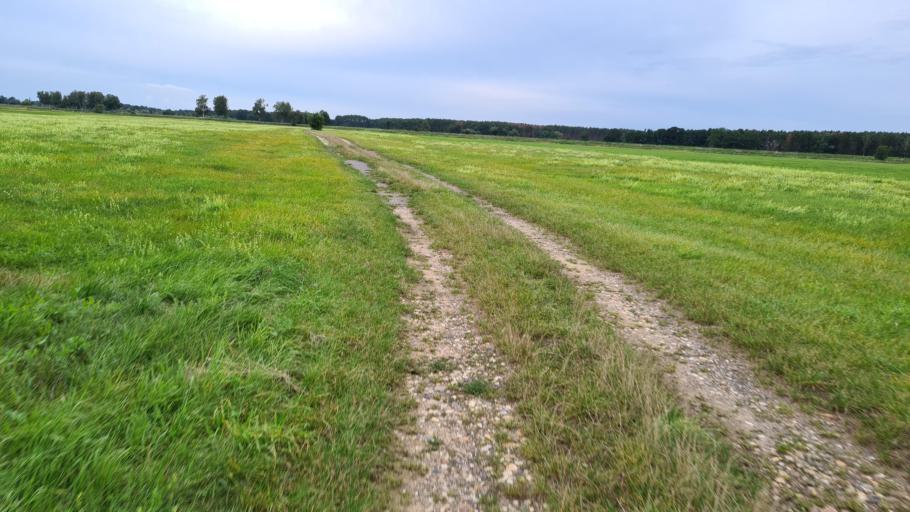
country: DE
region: Brandenburg
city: Bad Liebenwerda
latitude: 51.5297
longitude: 13.3764
